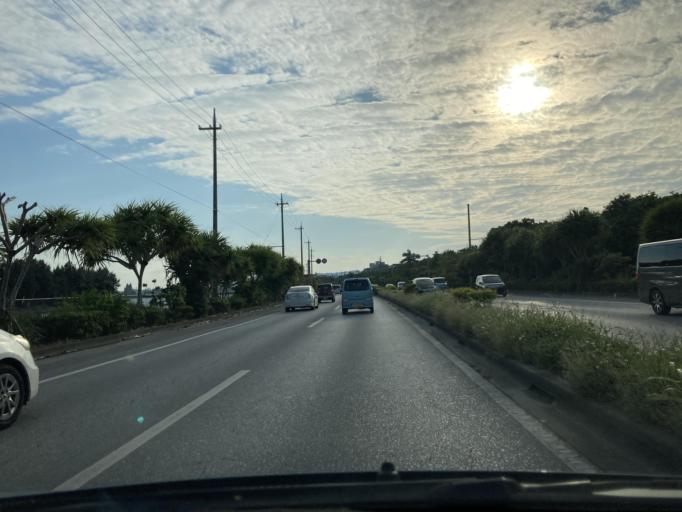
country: JP
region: Okinawa
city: Katsuren-haebaru
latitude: 26.3317
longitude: 127.8380
